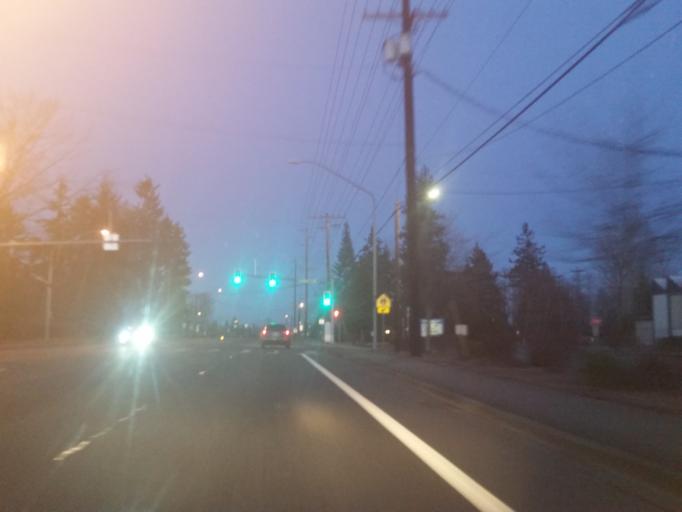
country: US
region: Washington
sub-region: Snohomish County
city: Martha Lake
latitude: 47.8947
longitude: -122.2698
